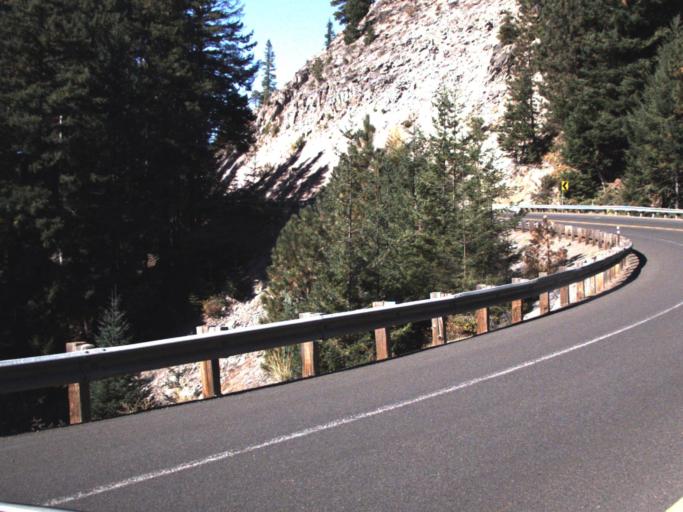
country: US
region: Washington
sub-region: Yakima County
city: Tieton
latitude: 46.6530
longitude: -121.2957
